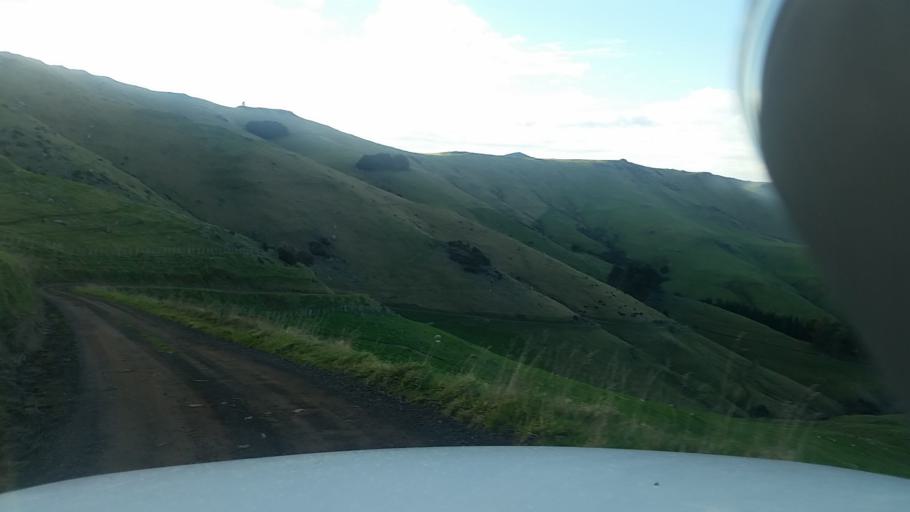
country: NZ
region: Canterbury
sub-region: Christchurch City
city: Christchurch
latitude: -43.7266
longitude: 172.9536
